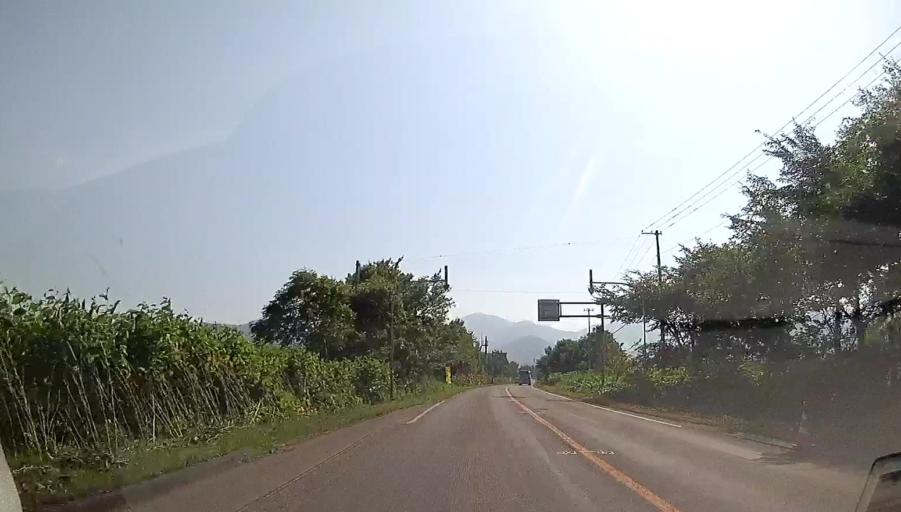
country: JP
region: Hokkaido
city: Otofuke
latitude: 42.9956
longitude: 142.8539
